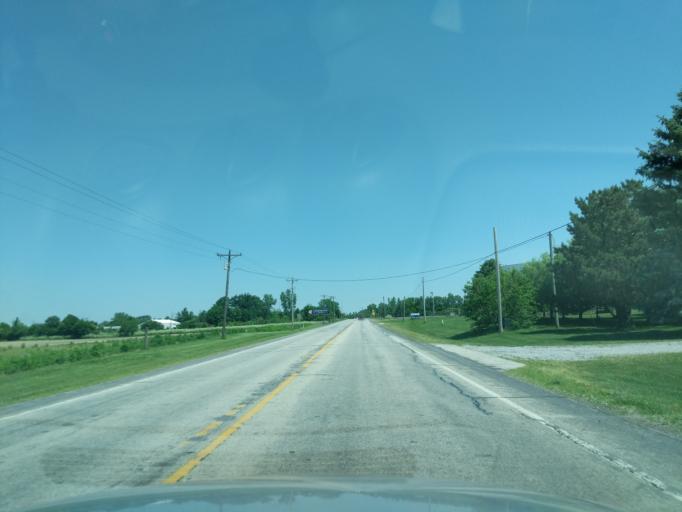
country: US
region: Indiana
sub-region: Whitley County
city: Columbia City
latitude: 41.0833
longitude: -85.4701
